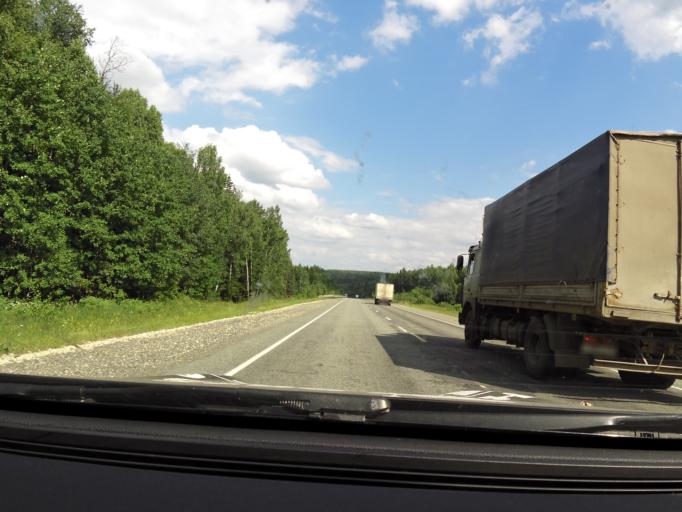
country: RU
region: Sverdlovsk
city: Bisert'
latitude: 56.8291
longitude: 59.0914
